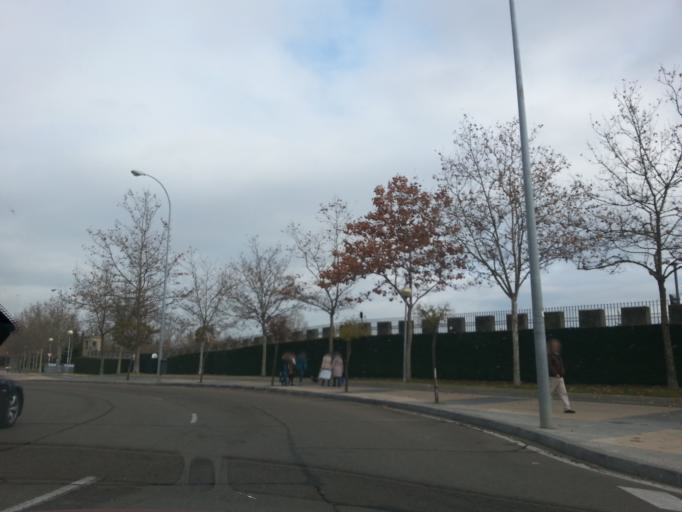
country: ES
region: Castille and Leon
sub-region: Provincia de Salamanca
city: Salamanca
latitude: 40.9771
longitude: -5.6670
